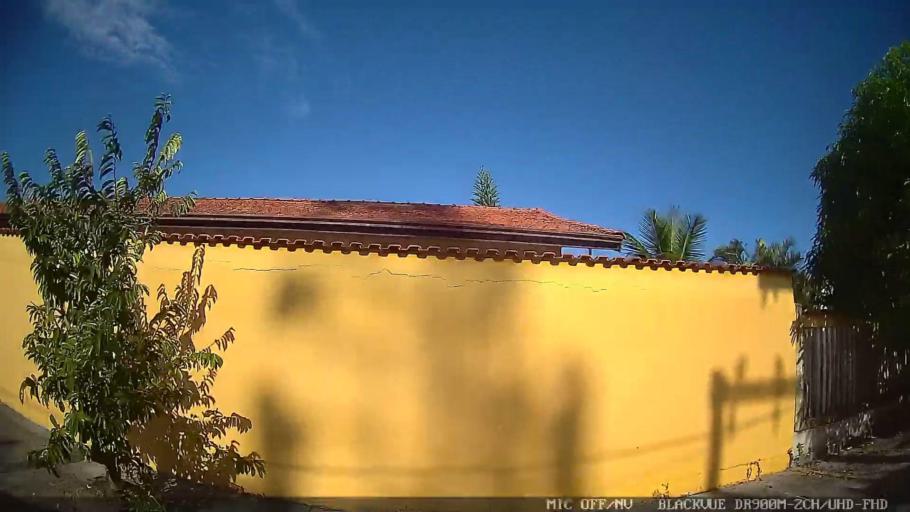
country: BR
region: Sao Paulo
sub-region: Itanhaem
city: Itanhaem
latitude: -24.2137
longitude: -46.8470
